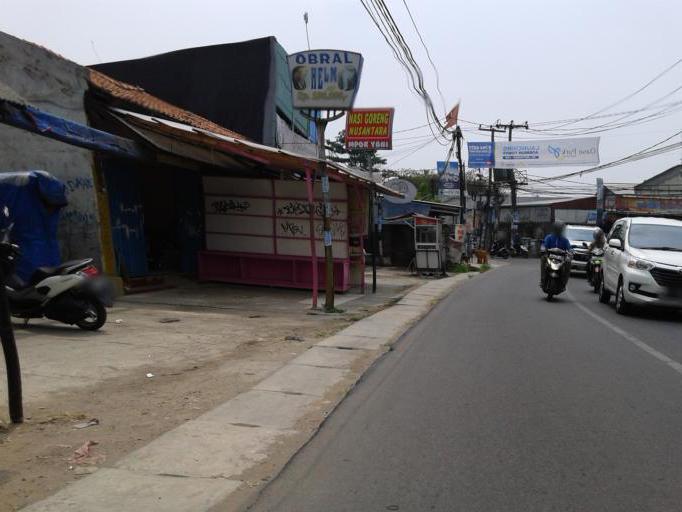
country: ID
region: Banten
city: South Tangerang
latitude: -6.2964
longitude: 106.7580
